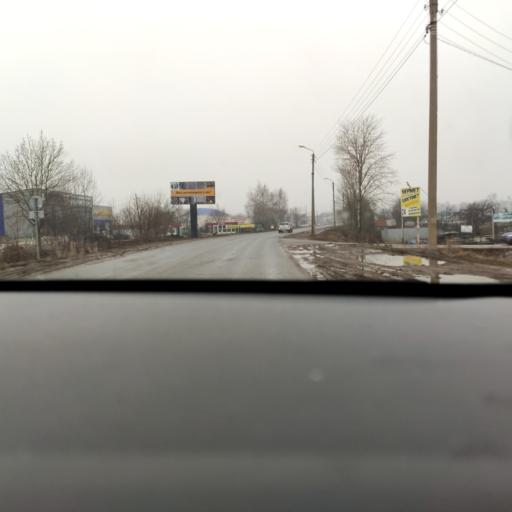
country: RU
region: Tatarstan
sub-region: Chistopol'skiy Rayon
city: Chistopol'
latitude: 55.3444
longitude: 50.6500
